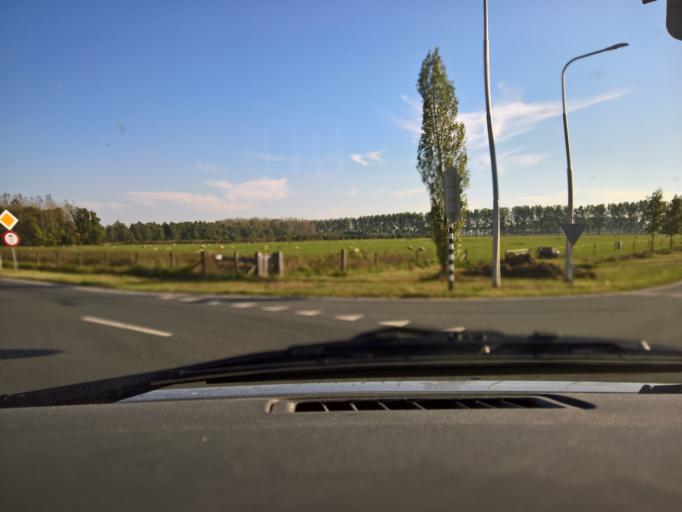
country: NL
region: Gelderland
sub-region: Gemeente Druten
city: Druten
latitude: 51.8725
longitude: 5.5337
